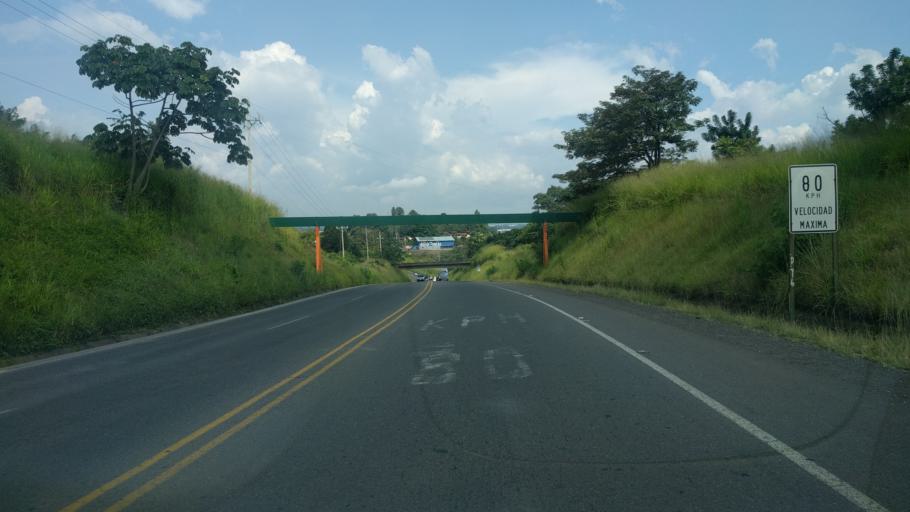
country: CR
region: Alajuela
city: Atenas
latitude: 10.0165
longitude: -84.3542
